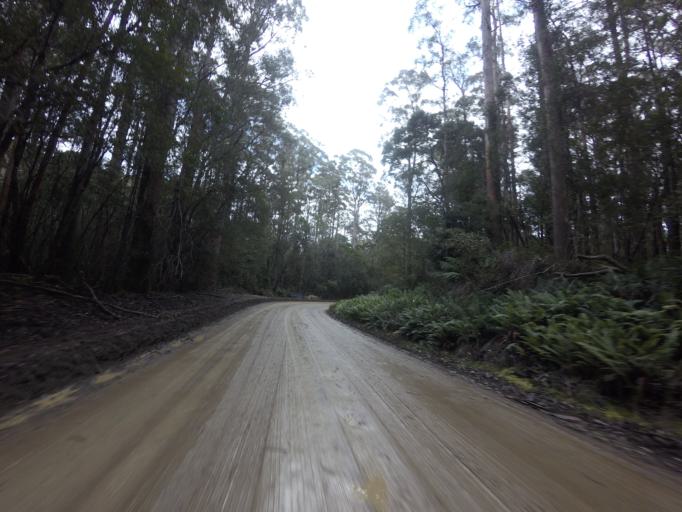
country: AU
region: Tasmania
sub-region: Huon Valley
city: Geeveston
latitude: -43.4170
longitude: 146.8782
